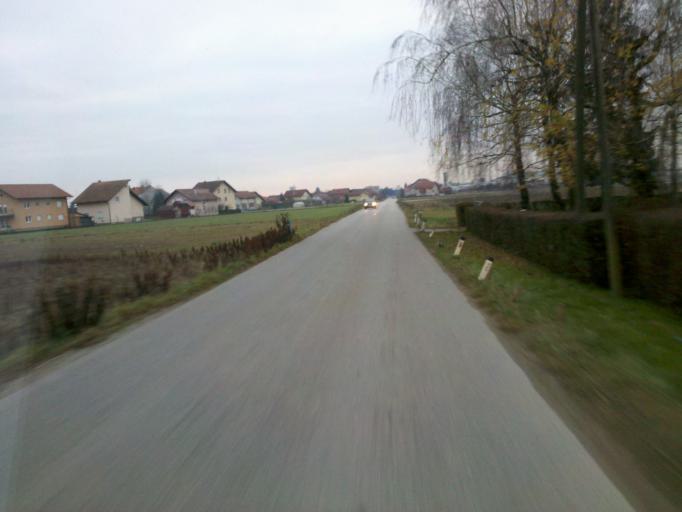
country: HR
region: Grad Zagreb
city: Lucko
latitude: 45.7582
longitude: 15.8717
